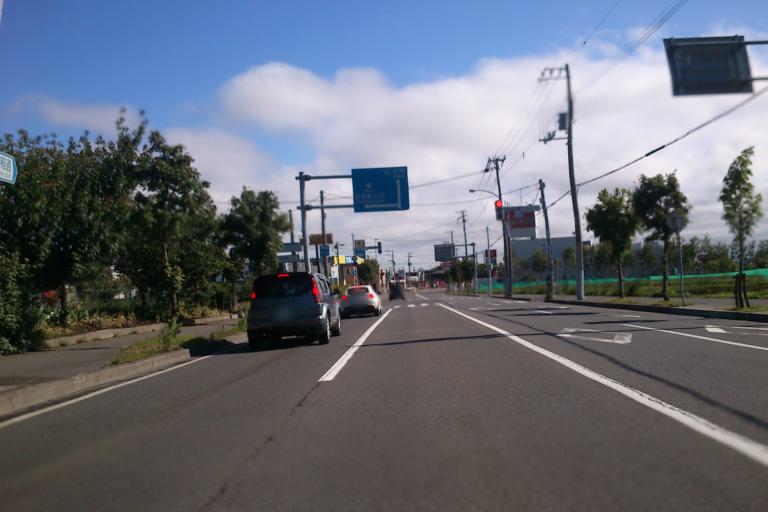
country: JP
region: Hokkaido
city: Sapporo
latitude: 43.1202
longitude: 141.2481
